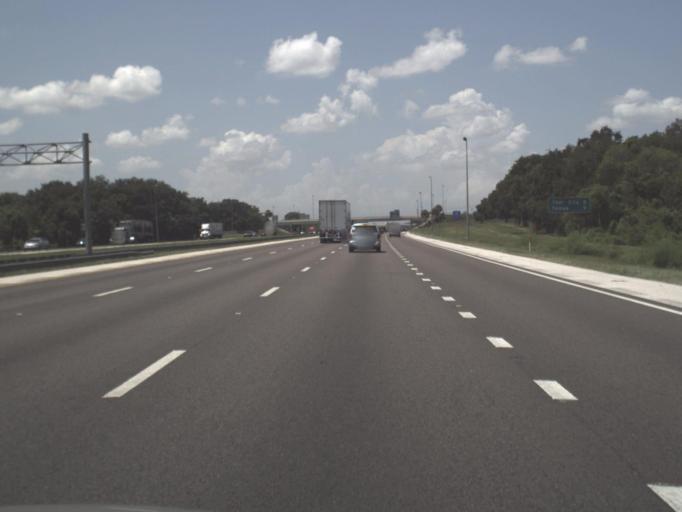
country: US
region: Florida
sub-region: Hillsborough County
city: Mango
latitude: 28.0042
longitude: -82.3140
